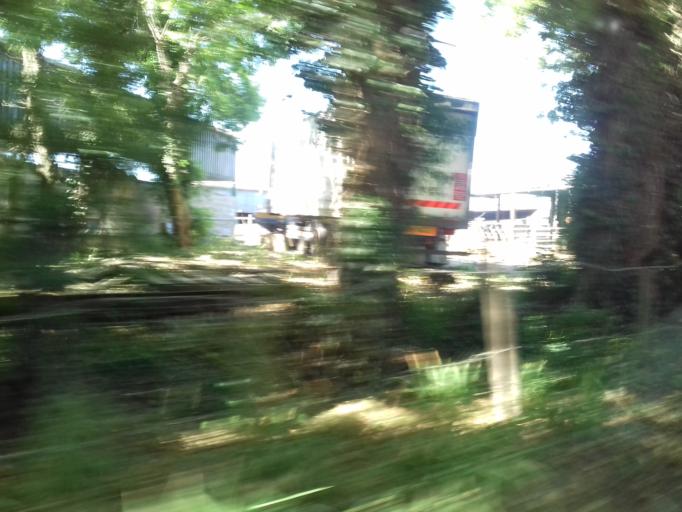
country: IE
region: Leinster
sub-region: Dublin City
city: Finglas
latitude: 53.4357
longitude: -6.3015
